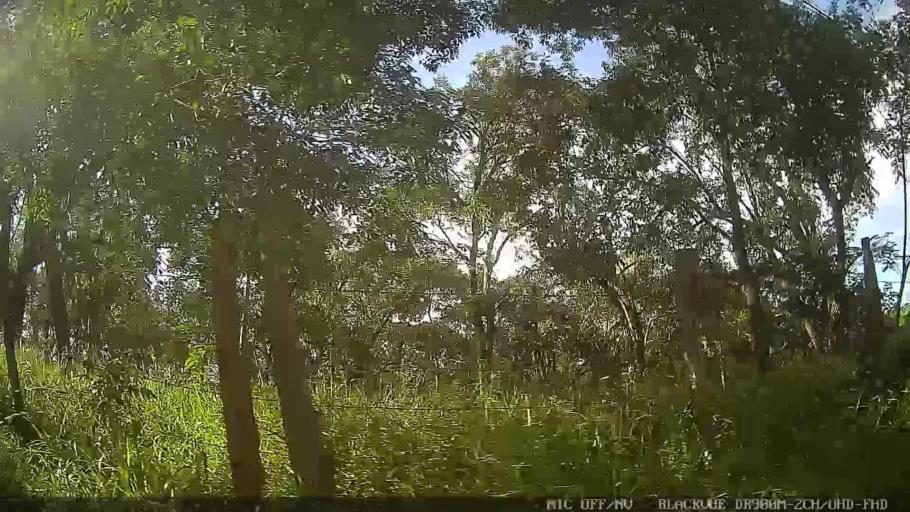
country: BR
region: Sao Paulo
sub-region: Tiete
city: Tiete
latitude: -23.0859
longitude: -47.6913
